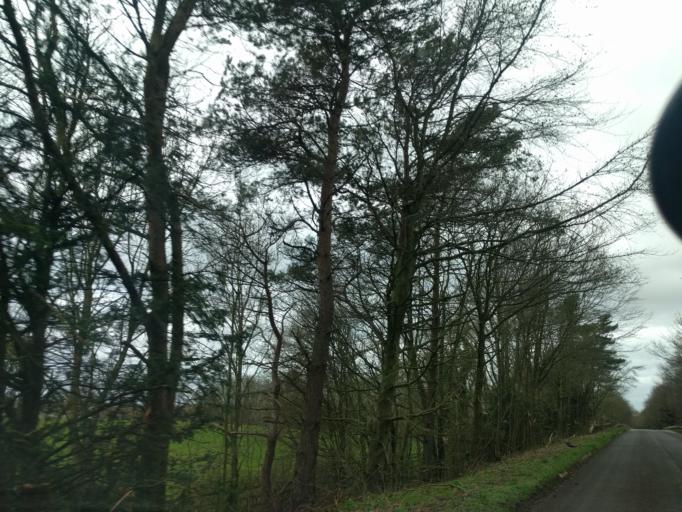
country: GB
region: England
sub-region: Wiltshire
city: Biddestone
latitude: 51.5095
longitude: -2.2002
